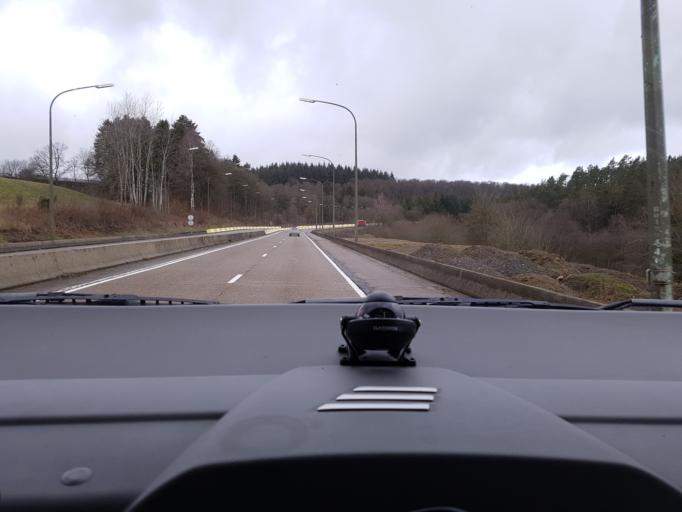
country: BE
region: Wallonia
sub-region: Province du Luxembourg
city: Tenneville
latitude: 50.0930
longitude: 5.4921
